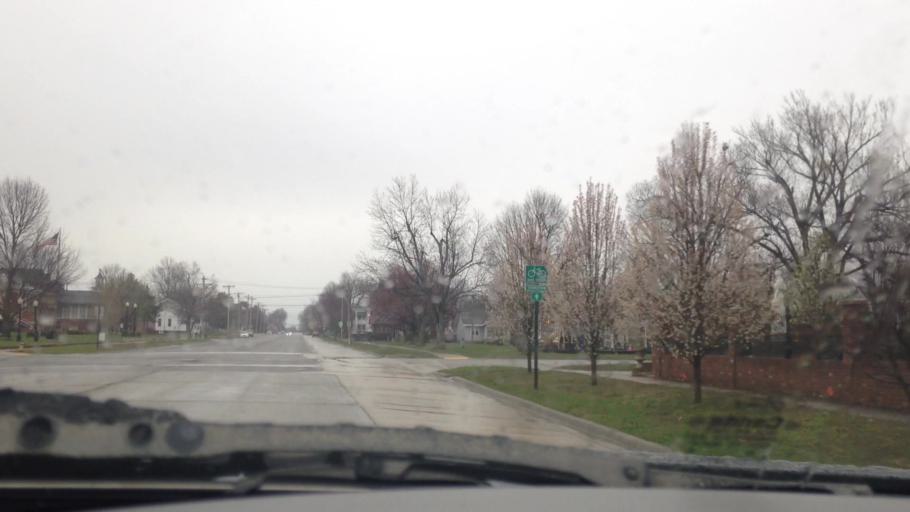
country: US
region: Illinois
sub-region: Massac County
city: Metropolis
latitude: 37.1482
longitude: -88.7325
